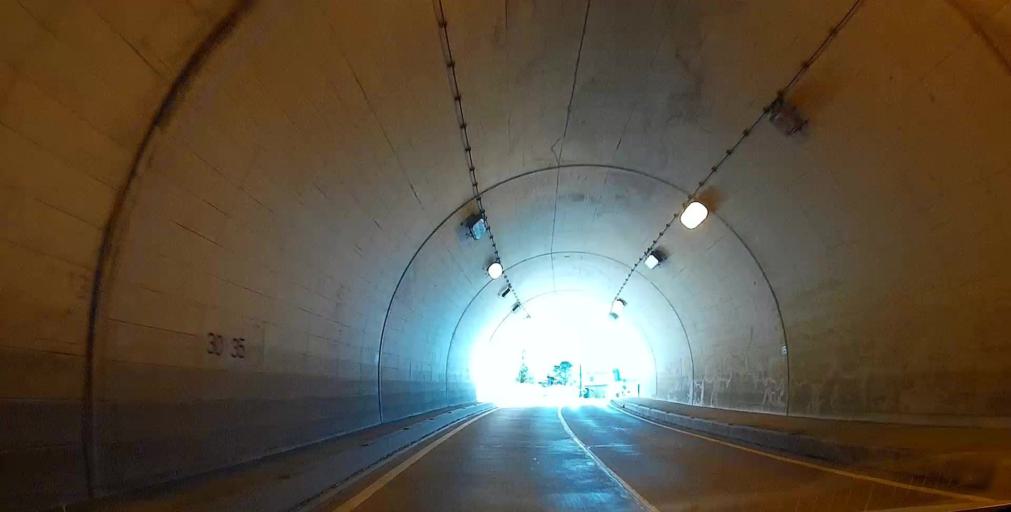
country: JP
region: Yamanashi
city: Fujikawaguchiko
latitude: 35.4893
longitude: 138.8212
